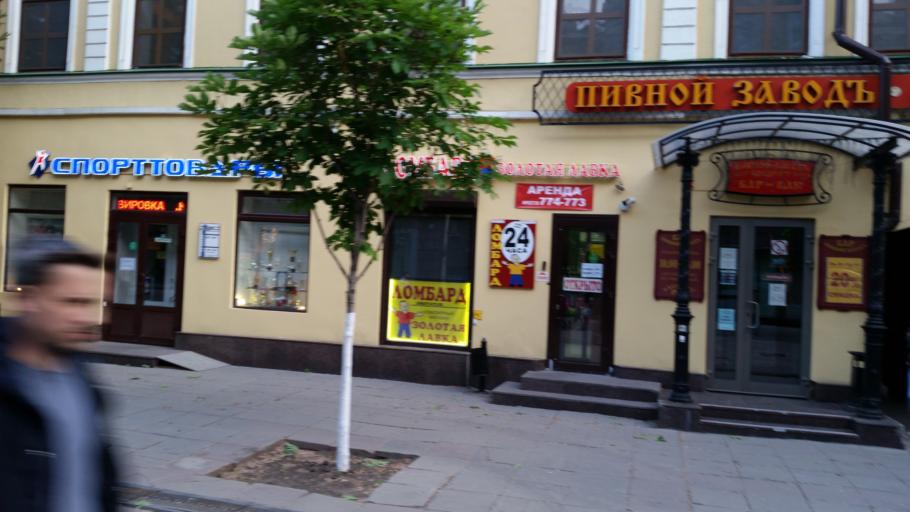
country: RU
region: Saratov
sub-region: Saratovskiy Rayon
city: Saratov
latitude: 51.5303
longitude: 46.0330
